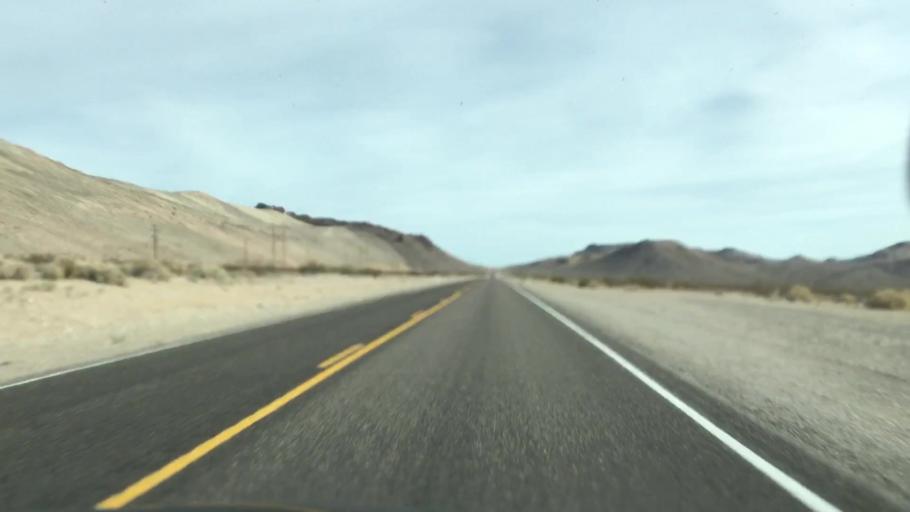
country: US
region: Nevada
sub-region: Nye County
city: Beatty
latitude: 36.8865
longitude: -116.8107
